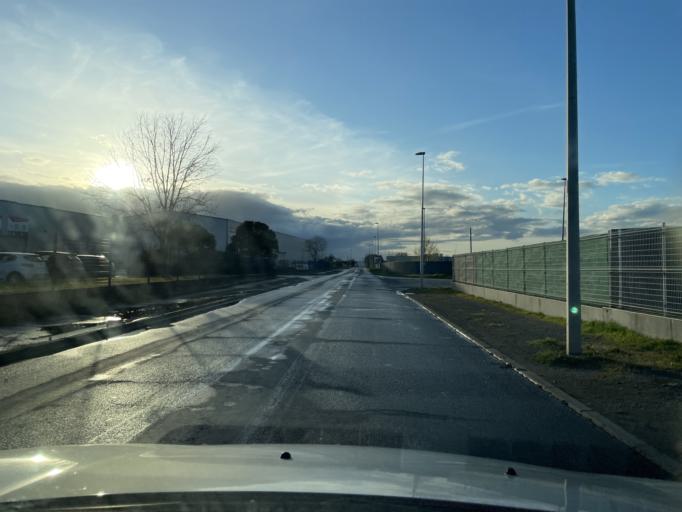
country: FR
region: Midi-Pyrenees
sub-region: Departement de la Haute-Garonne
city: Tournefeuille
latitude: 43.5998
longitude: 1.3117
